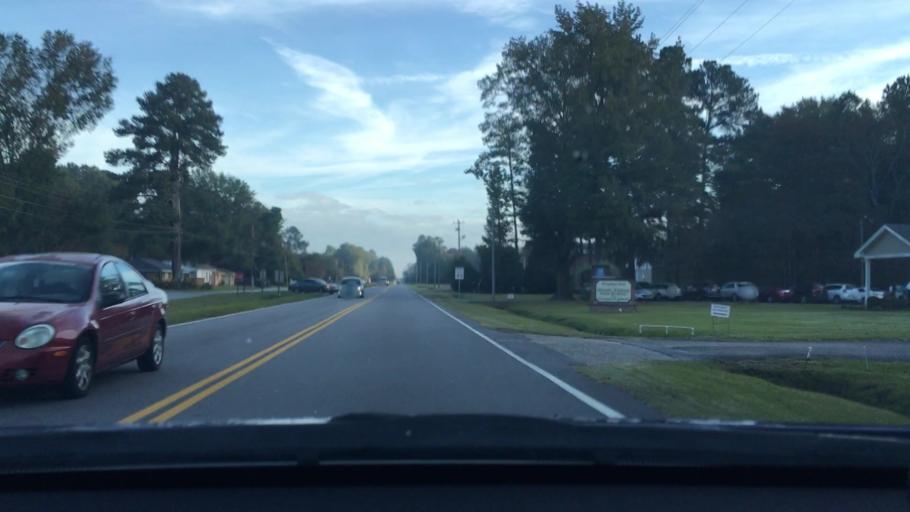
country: US
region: South Carolina
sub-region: Sumter County
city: Sumter
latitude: 33.9277
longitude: -80.3261
